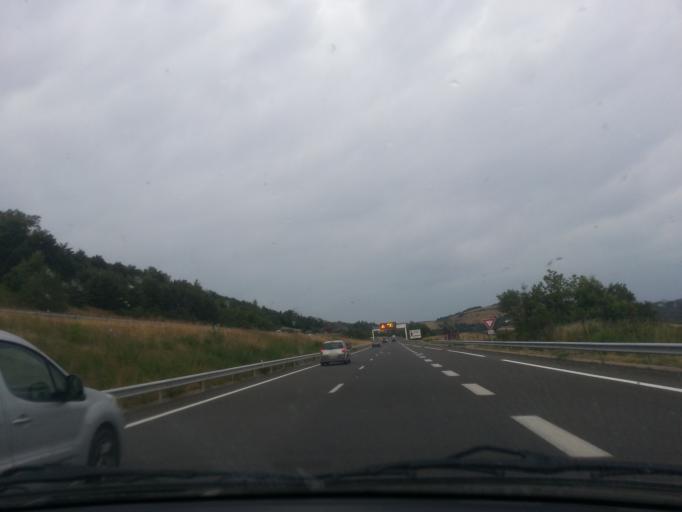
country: FR
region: Languedoc-Roussillon
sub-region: Departement de la Lozere
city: Marvejols
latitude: 44.5610
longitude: 3.2542
